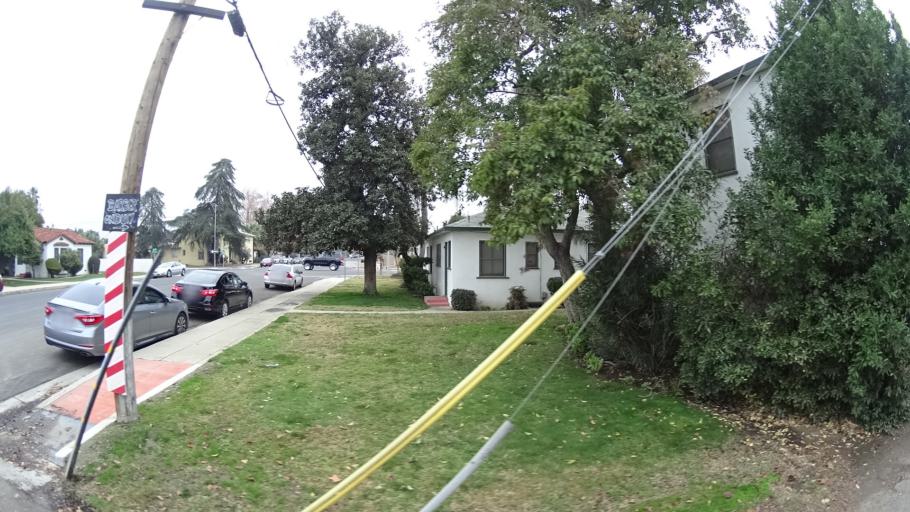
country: US
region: California
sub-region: Kern County
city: Bakersfield
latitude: 35.3806
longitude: -119.0260
